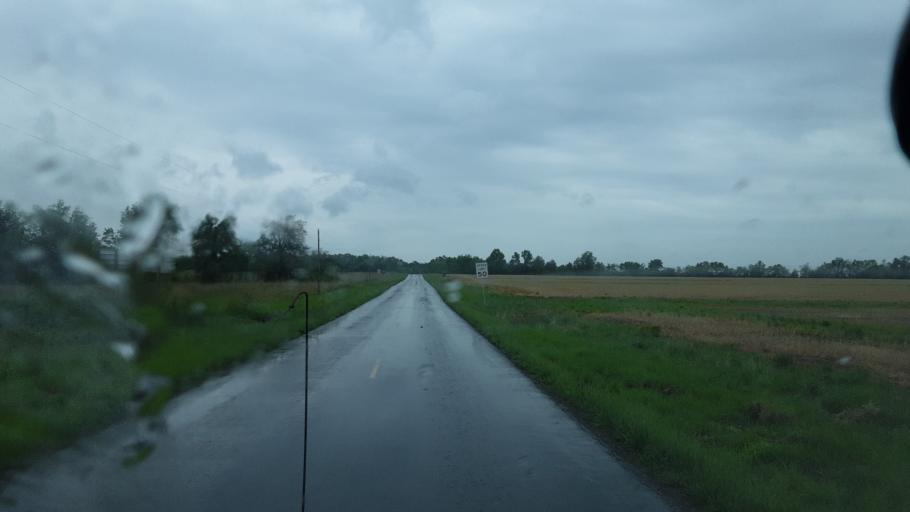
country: US
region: Missouri
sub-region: Randolph County
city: Moberly
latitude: 39.3920
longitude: -92.2483
